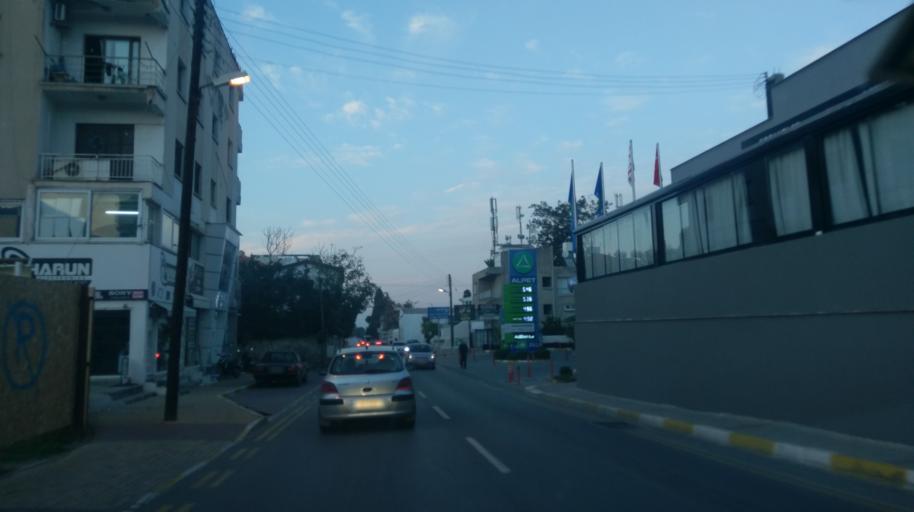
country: CY
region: Keryneia
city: Kyrenia
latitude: 35.3348
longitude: 33.3198
